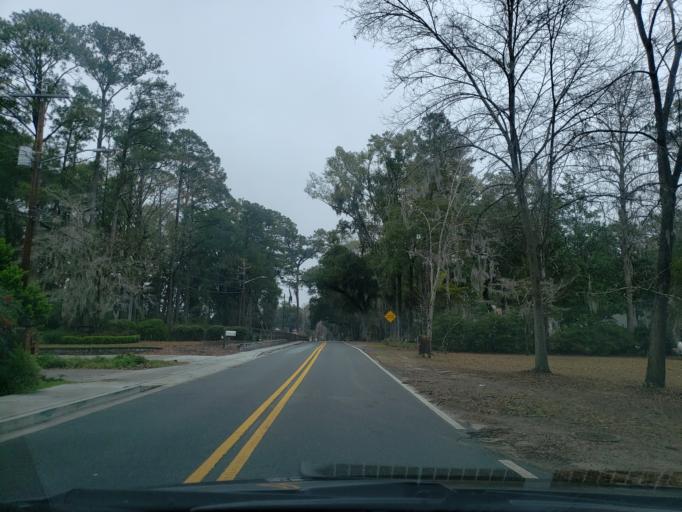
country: US
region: Georgia
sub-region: Chatham County
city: Montgomery
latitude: 31.9375
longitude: -81.1530
